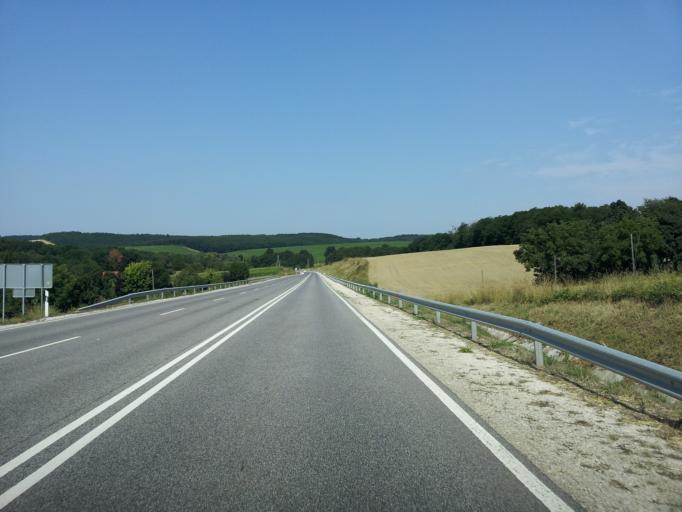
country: HU
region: Zala
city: Zalaszentgrot
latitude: 46.8342
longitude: 17.0409
